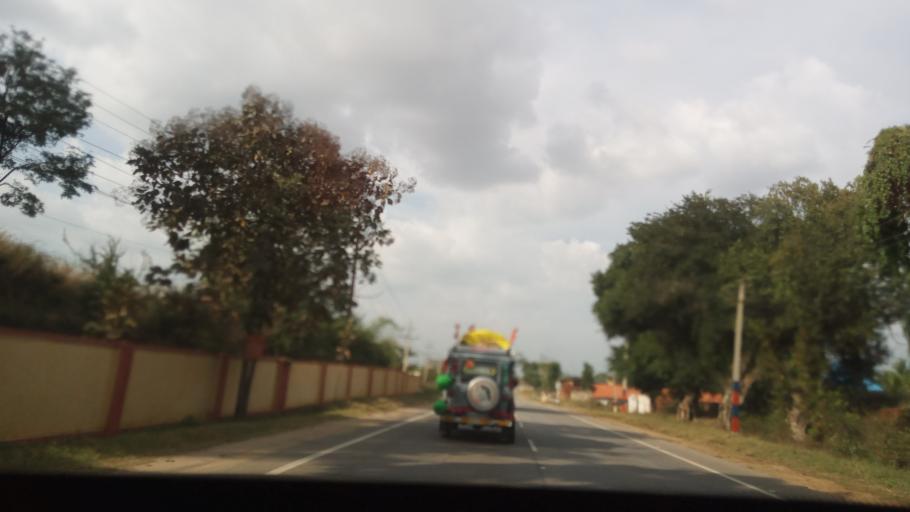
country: IN
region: Karnataka
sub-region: Tumkur
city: Kunigal
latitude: 12.8416
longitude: 77.0354
